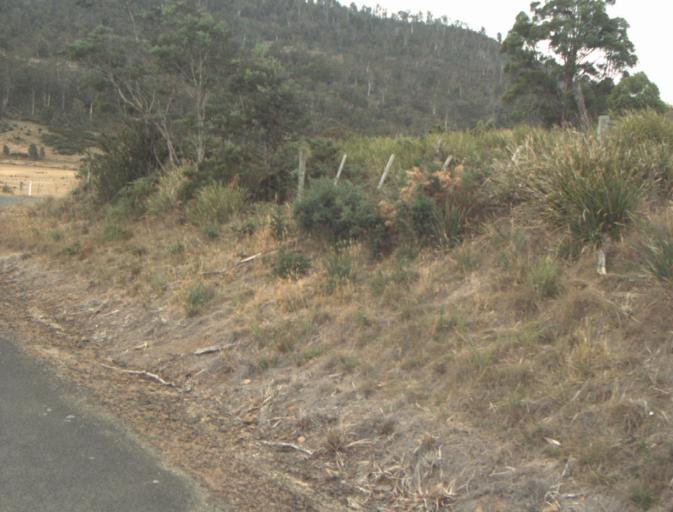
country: AU
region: Tasmania
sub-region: Northern Midlands
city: Evandale
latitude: -41.4882
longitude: 147.4383
